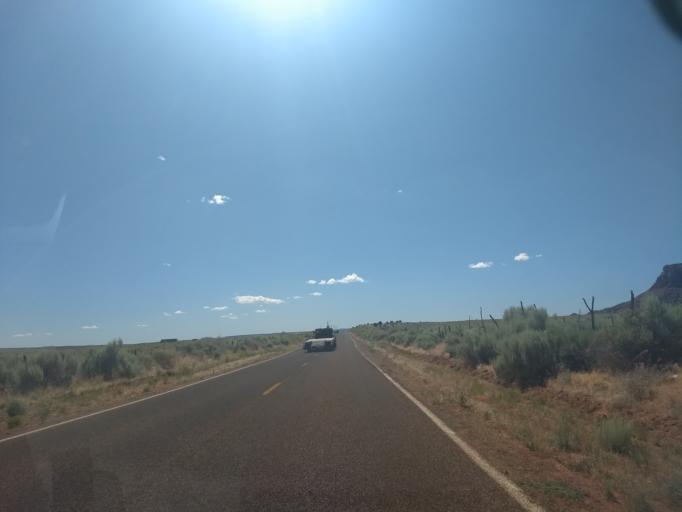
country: US
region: Arizona
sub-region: Mohave County
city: Colorado City
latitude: 36.9469
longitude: -112.9110
